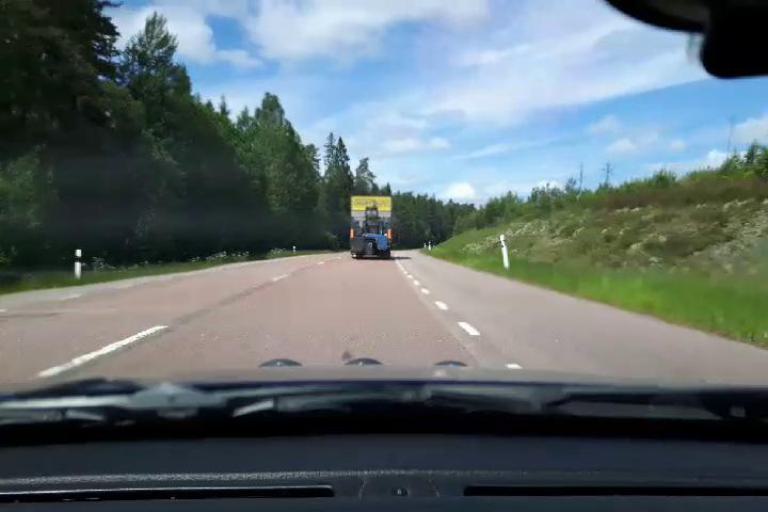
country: SE
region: Uppsala
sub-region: Osthammars Kommun
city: Bjorklinge
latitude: 60.1232
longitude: 17.5096
